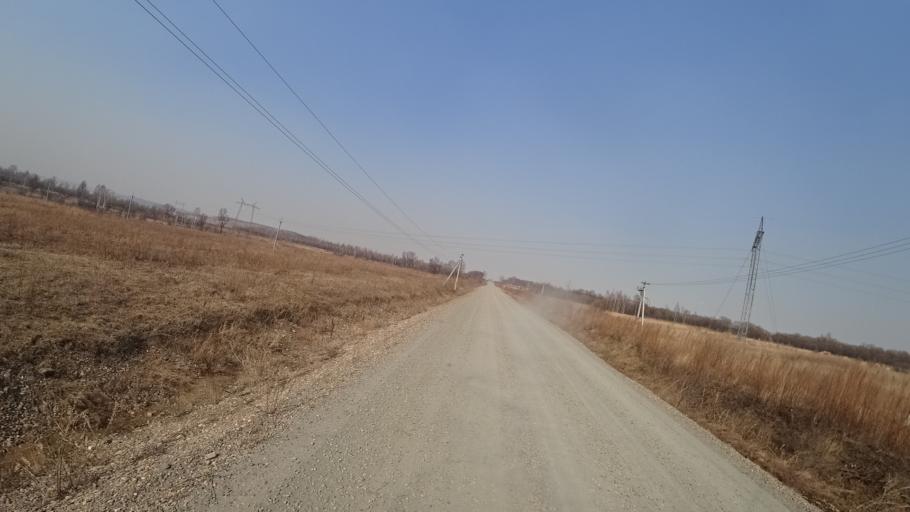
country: RU
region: Amur
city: Novobureyskiy
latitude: 49.8142
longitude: 129.9737
